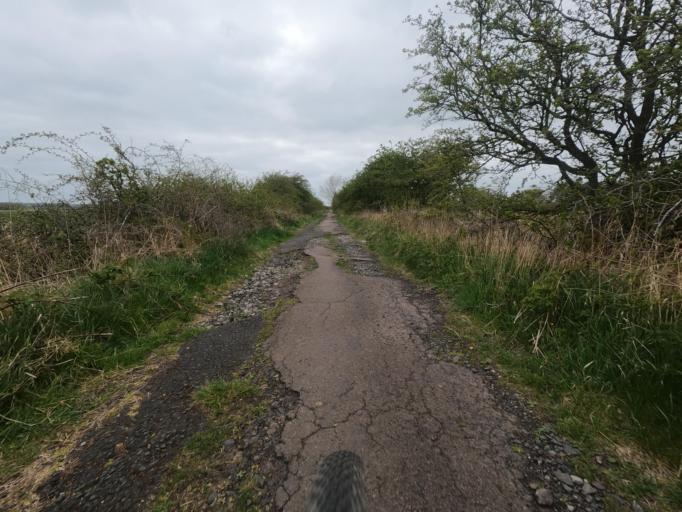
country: GB
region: England
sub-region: Newcastle upon Tyne
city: Dinnington
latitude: 55.0565
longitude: -1.7031
